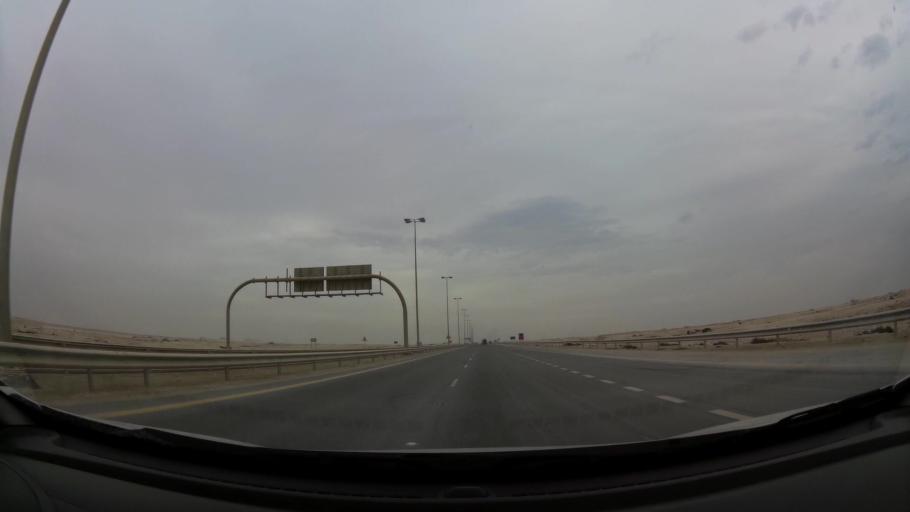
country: BH
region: Central Governorate
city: Dar Kulayb
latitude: 25.9993
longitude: 50.6046
